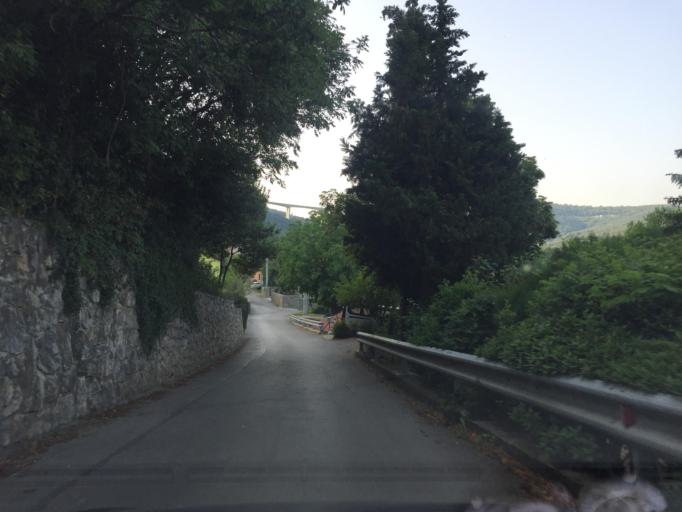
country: IT
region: Friuli Venezia Giulia
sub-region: Provincia di Trieste
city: Dolina
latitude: 45.5722
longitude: 13.8567
